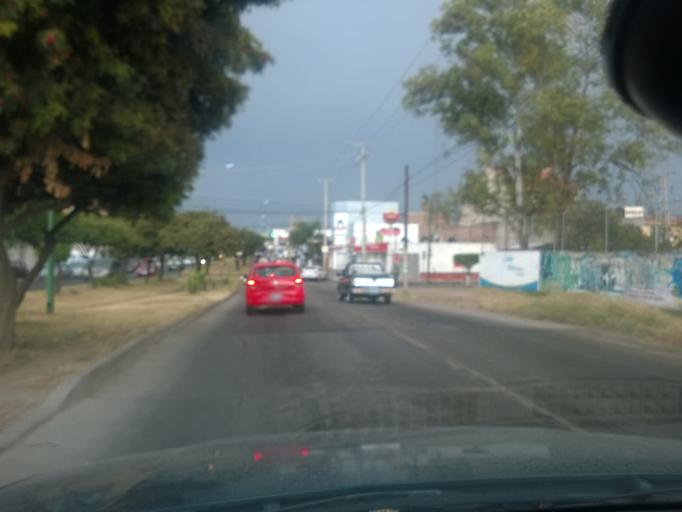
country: MX
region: Guanajuato
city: Leon
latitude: 21.1024
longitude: -101.6547
